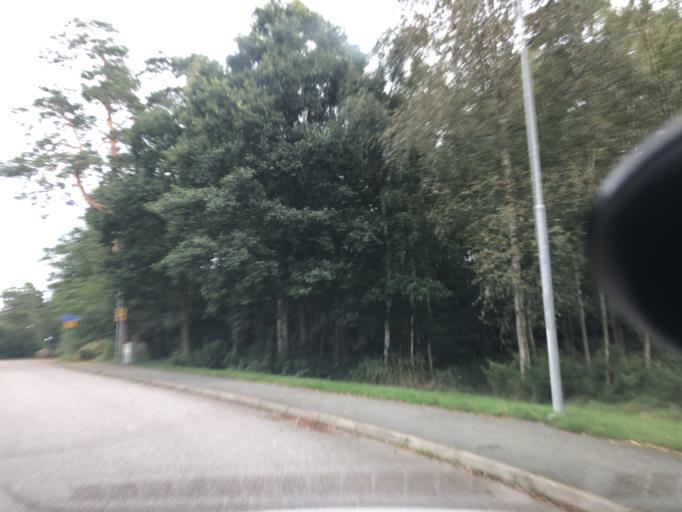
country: SE
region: Vaestra Goetaland
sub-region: Goteborg
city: Goeteborg
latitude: 57.7524
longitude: 11.9556
